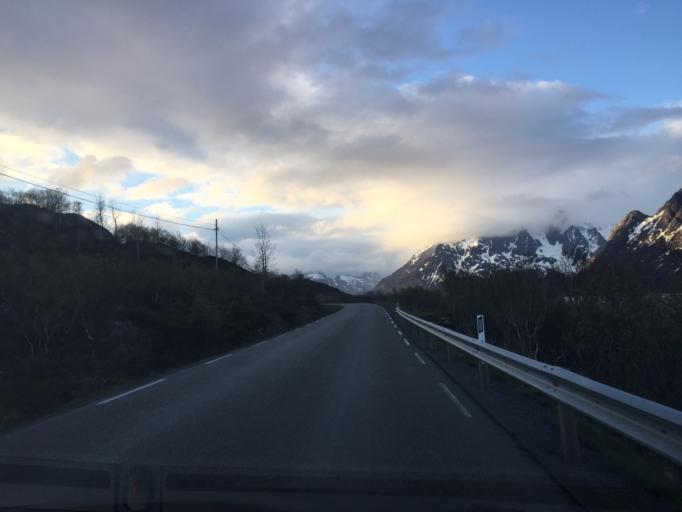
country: NO
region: Nordland
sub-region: Vagan
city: Svolvaer
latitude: 68.2887
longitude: 14.6954
